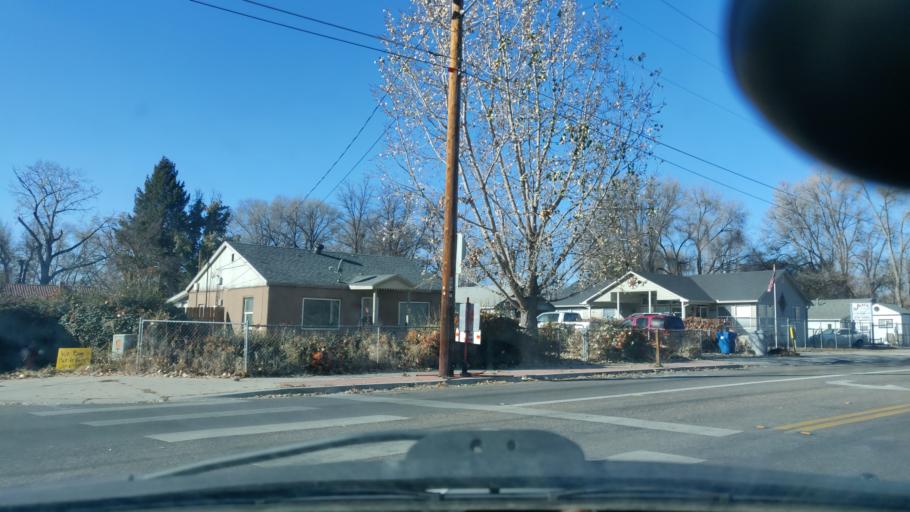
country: US
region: Idaho
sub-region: Ada County
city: Garden City
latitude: 43.6370
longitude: -116.2506
